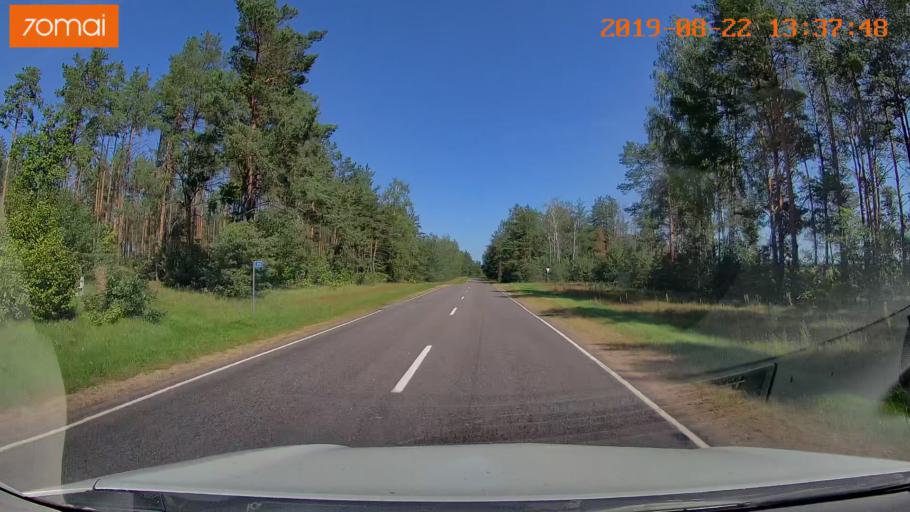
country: BY
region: Minsk
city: Staryya Darohi
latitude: 53.2179
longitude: 28.3066
